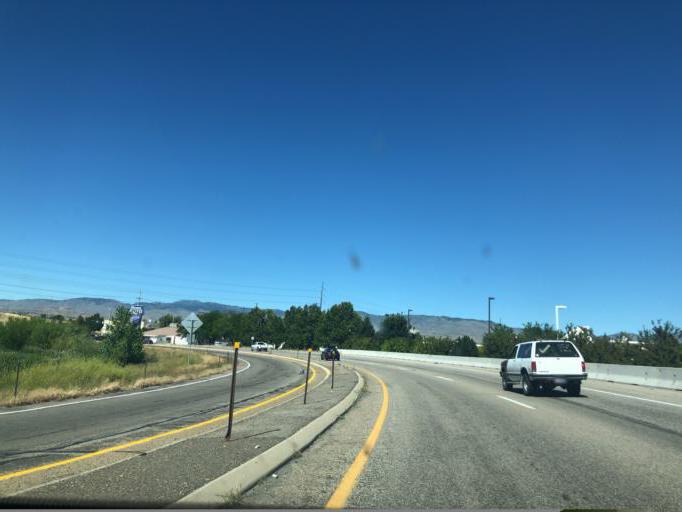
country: US
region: Idaho
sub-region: Ada County
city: Garden City
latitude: 43.6028
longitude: -116.2786
